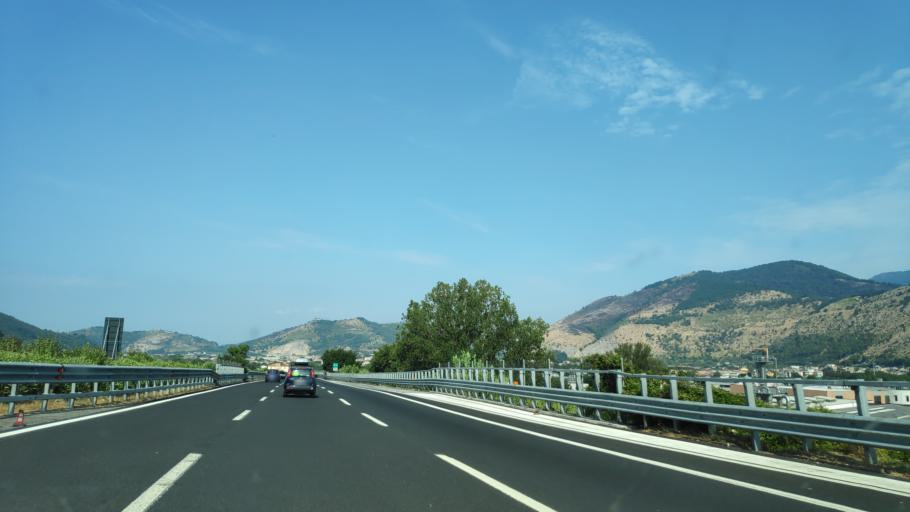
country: IT
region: Campania
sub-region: Provincia di Salerno
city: Roccapiemonte
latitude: 40.7672
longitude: 14.7026
